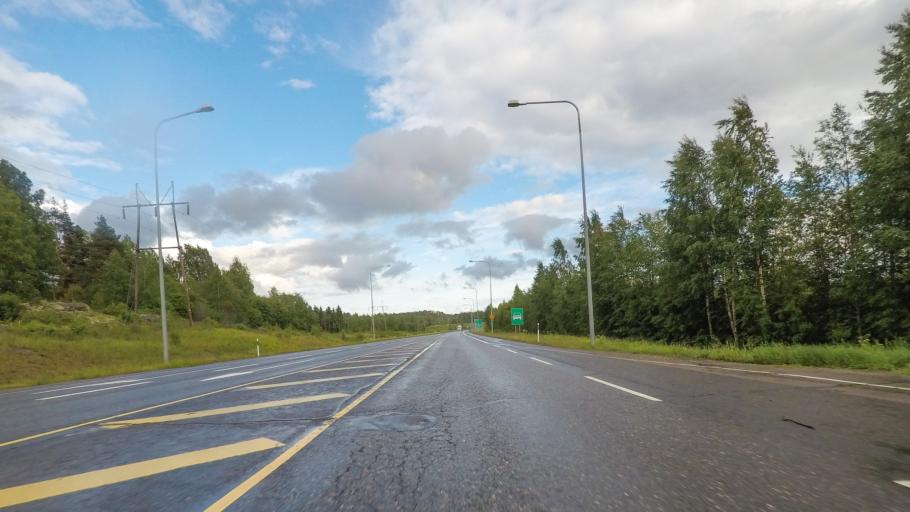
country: FI
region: Paijanne Tavastia
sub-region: Lahti
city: Heinola
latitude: 61.3017
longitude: 26.0598
